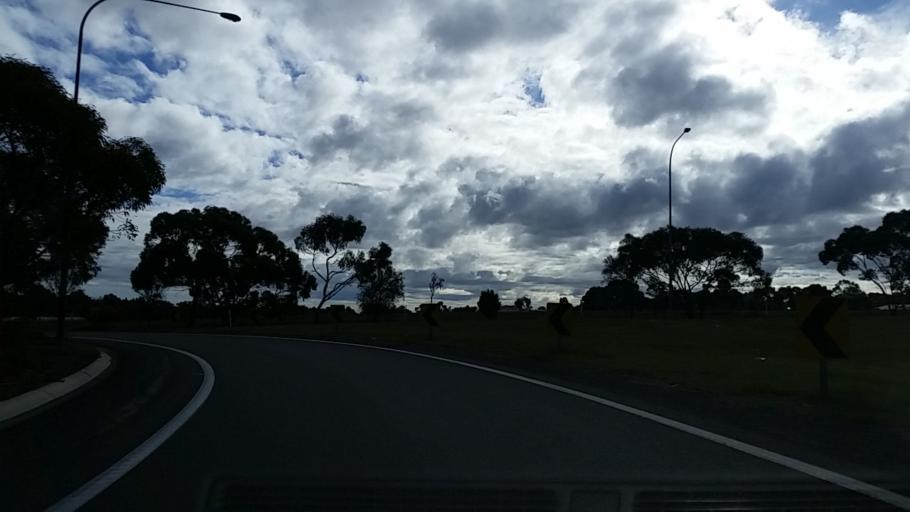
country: AU
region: South Australia
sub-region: Light
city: Willaston
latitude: -34.5779
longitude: 138.7386
